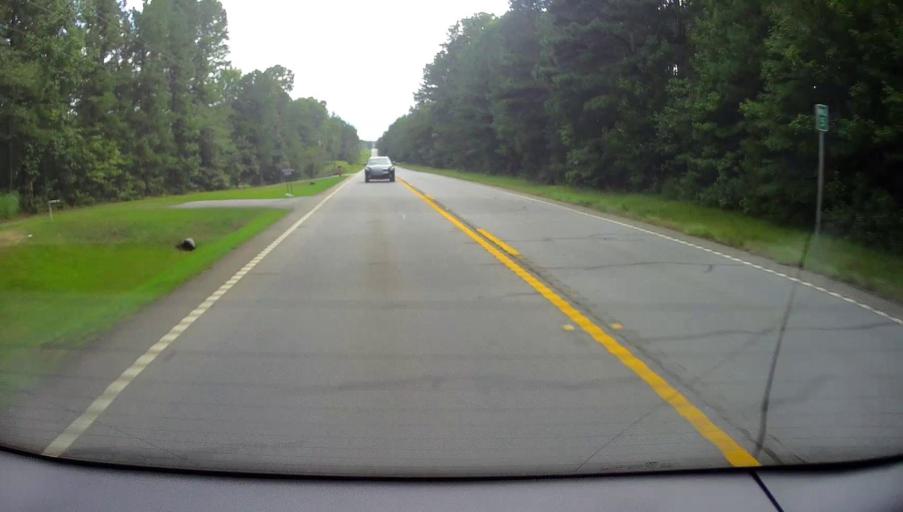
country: US
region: Georgia
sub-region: Coweta County
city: Senoia
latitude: 33.1510
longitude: -84.5865
